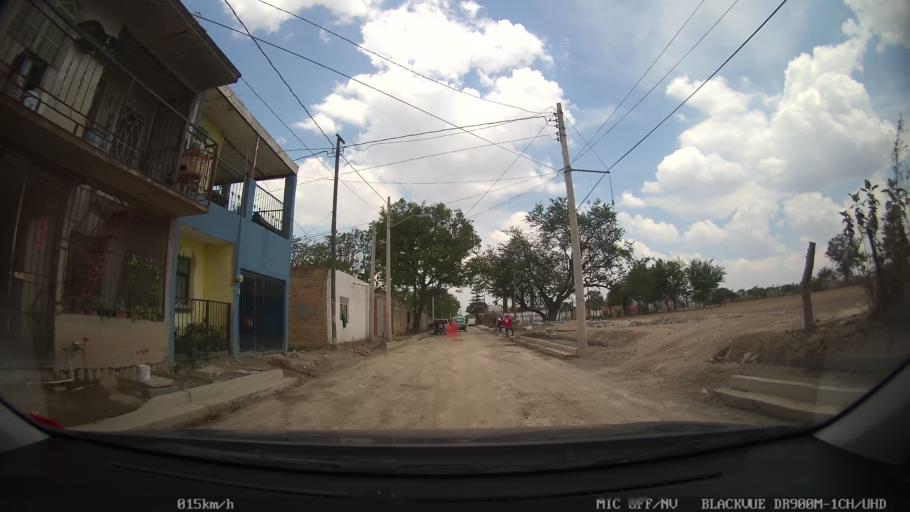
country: MX
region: Jalisco
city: Coyula
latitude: 20.6624
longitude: -103.2234
